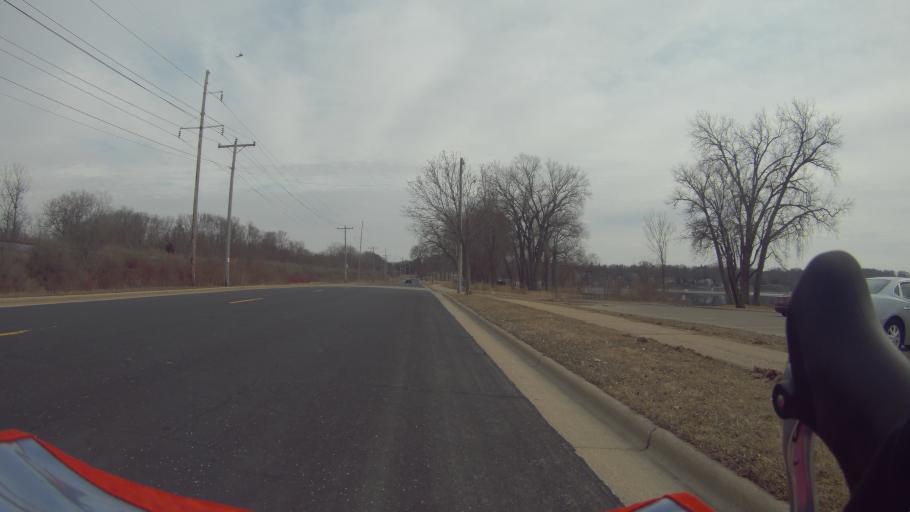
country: US
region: Wisconsin
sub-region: Dane County
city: Maple Bluff
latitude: 43.1277
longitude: -89.3784
